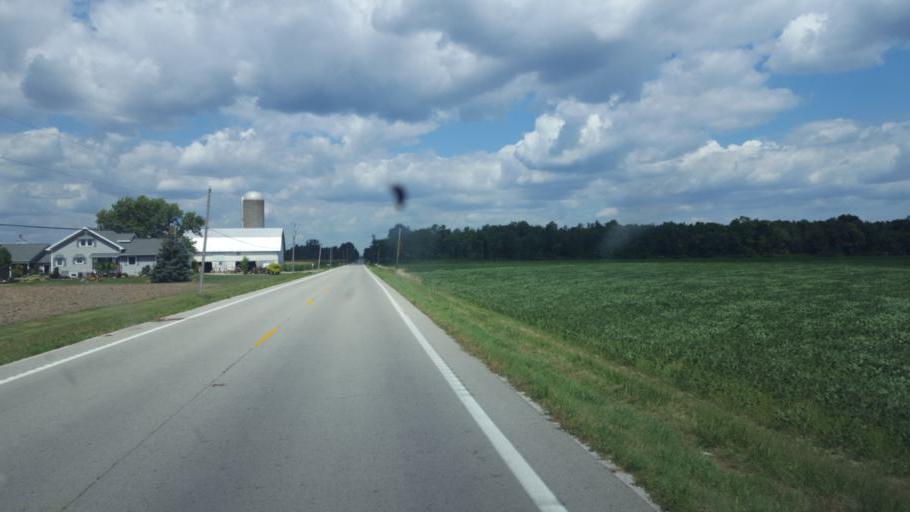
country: US
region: Ohio
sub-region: Sandusky County
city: Gibsonburg
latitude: 41.4103
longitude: -83.3192
